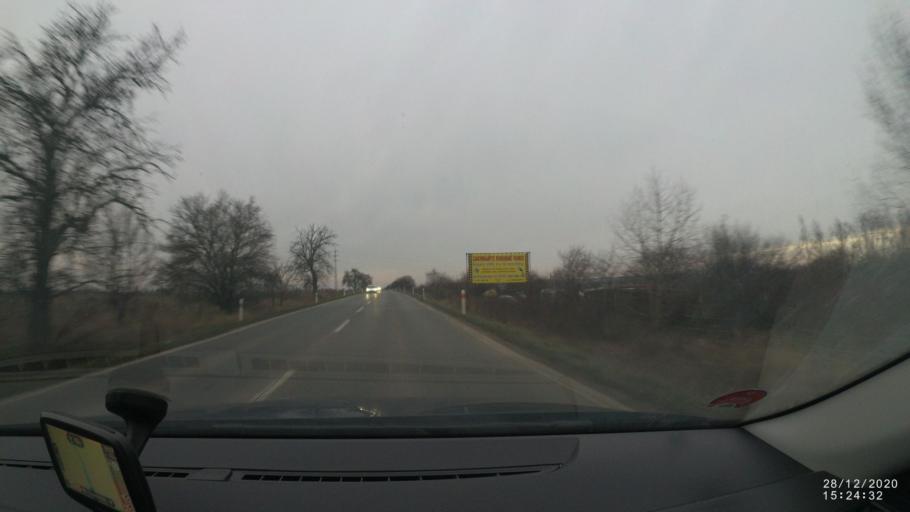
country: CZ
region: Praha
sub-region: Praha 20
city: Horni Pocernice
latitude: 50.0796
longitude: 14.6386
